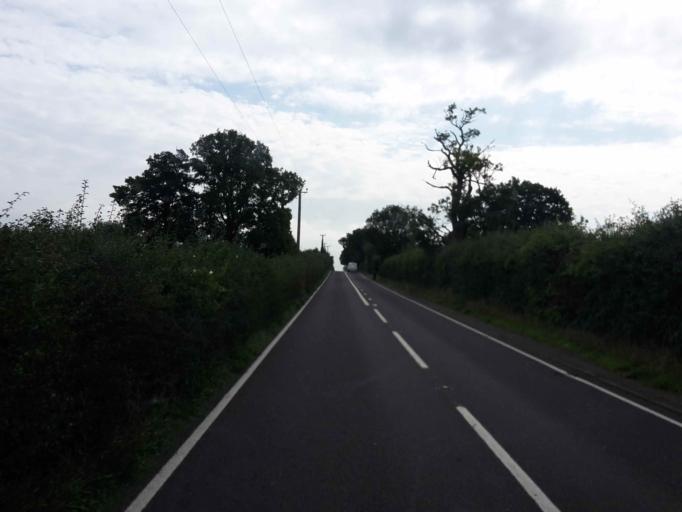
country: GB
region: England
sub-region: West Sussex
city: Billingshurst
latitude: 50.9983
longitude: -0.4187
